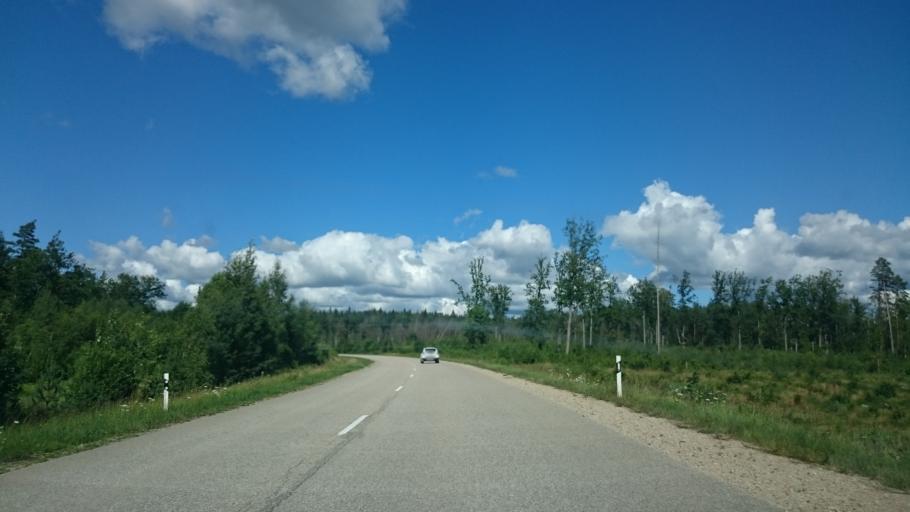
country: LV
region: Kuldigas Rajons
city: Kuldiga
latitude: 56.8788
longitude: 21.8737
